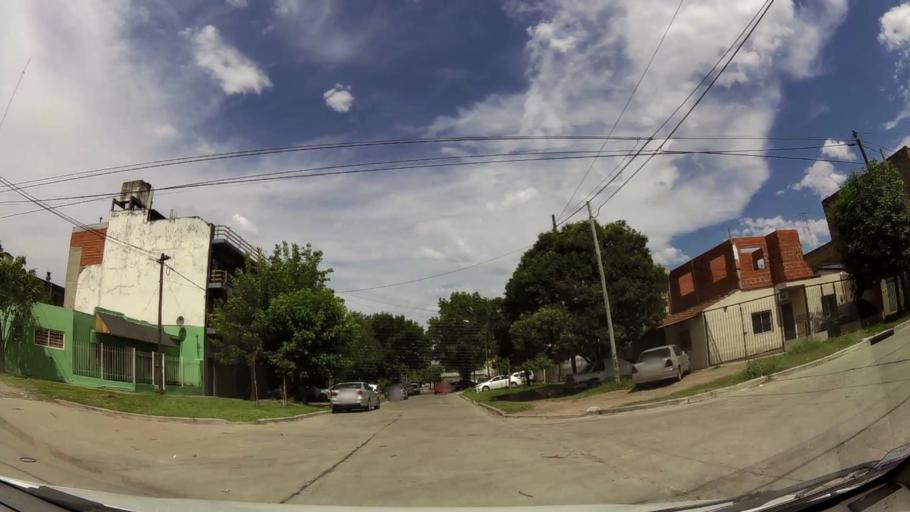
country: AR
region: Buenos Aires
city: San Justo
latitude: -34.6902
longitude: -58.5517
